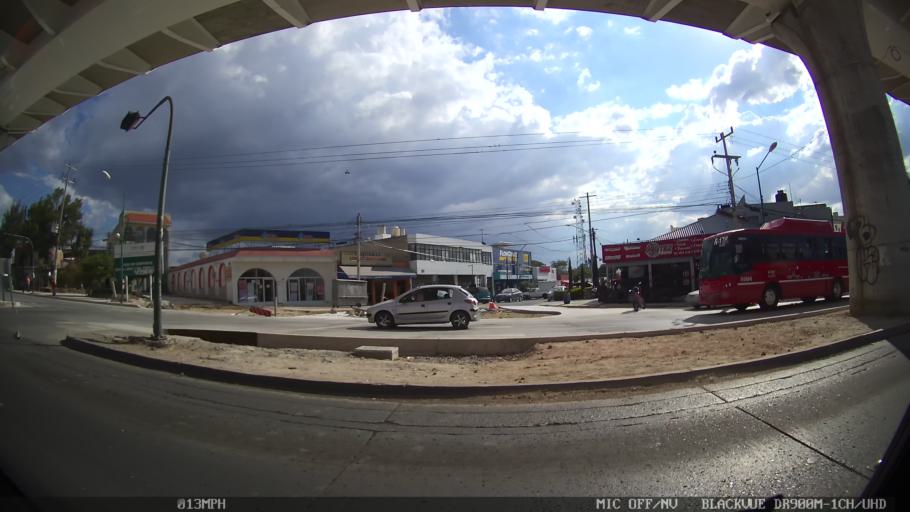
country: MX
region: Jalisco
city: Tlaquepaque
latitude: 20.6392
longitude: -103.3010
